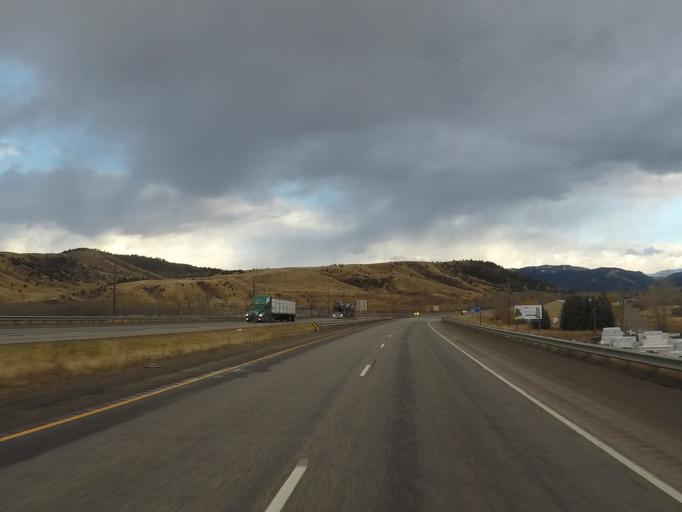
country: US
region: Montana
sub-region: Gallatin County
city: Bozeman
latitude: 45.6922
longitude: -111.0263
